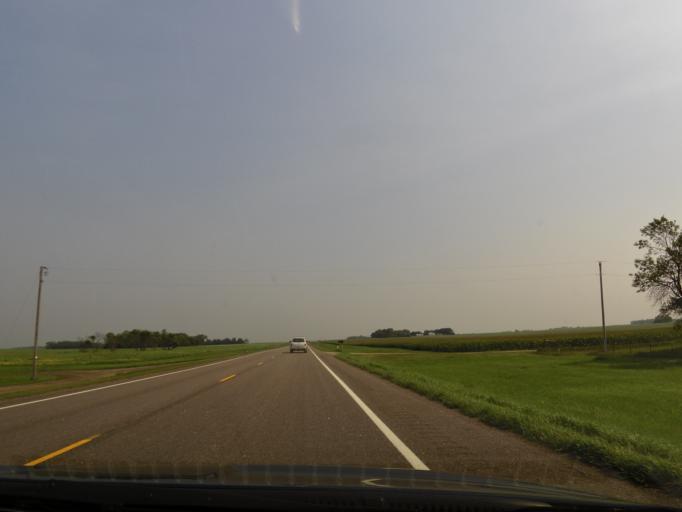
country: US
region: South Dakota
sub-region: Roberts County
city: Sisseton
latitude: 45.8486
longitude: -97.0743
